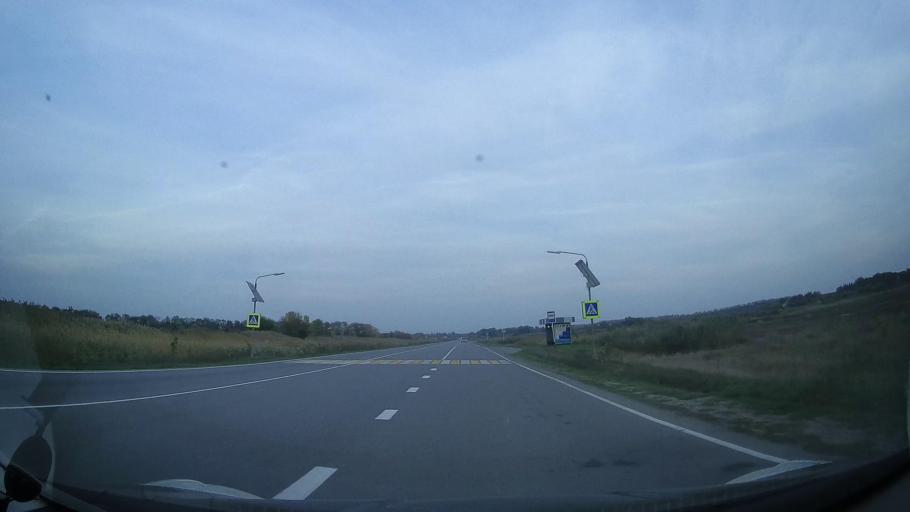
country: RU
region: Rostov
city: Ol'ginskaya
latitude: 47.1314
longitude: 39.9583
